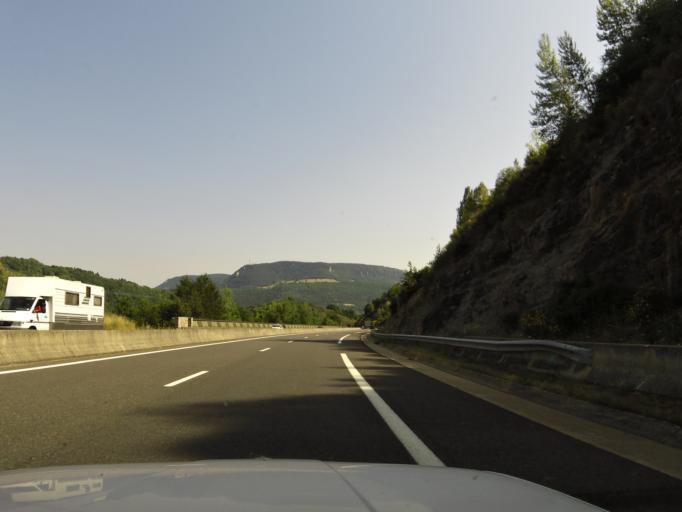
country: FR
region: Languedoc-Roussillon
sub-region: Departement de la Lozere
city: La Canourgue
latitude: 44.4509
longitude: 3.1931
